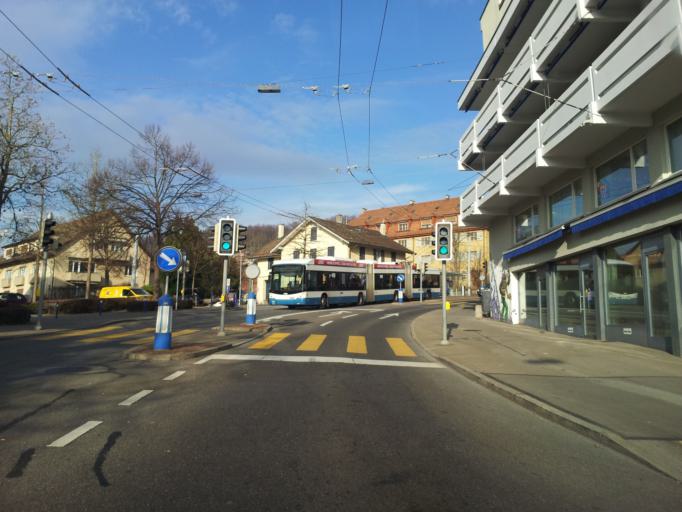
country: CH
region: Zurich
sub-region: Bezirk Zuerich
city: Zuerich (Kreis 6) / Unterstrass
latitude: 47.3953
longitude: 8.5323
